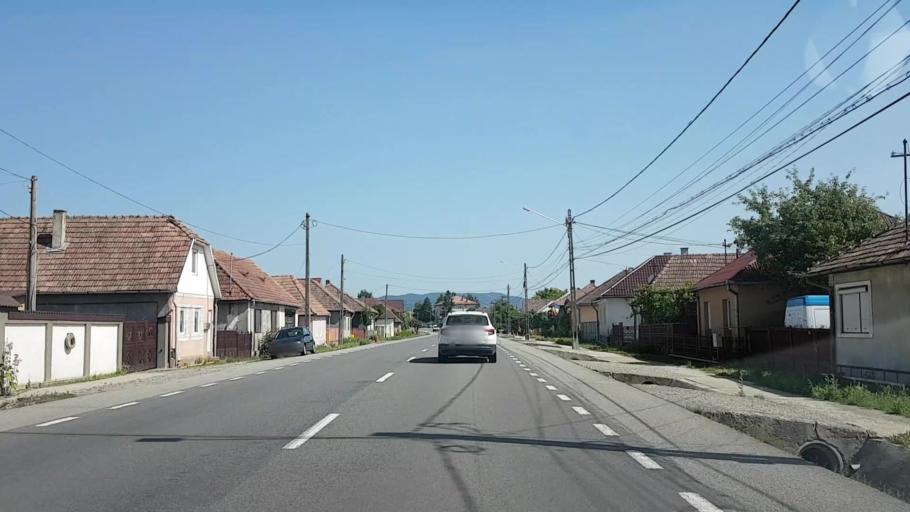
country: RO
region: Bistrita-Nasaud
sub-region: Comuna Sieu-Magherus
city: Sieu-Magherus
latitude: 47.0933
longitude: 24.3704
